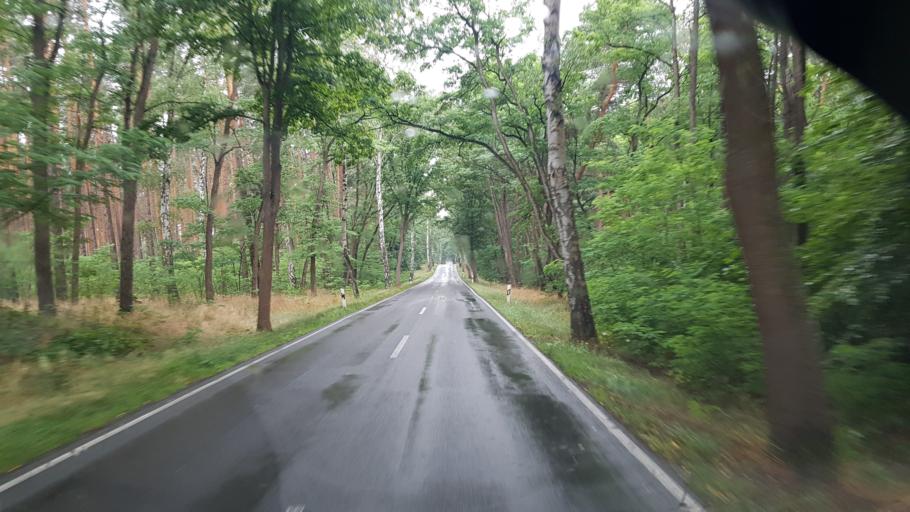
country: DE
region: Brandenburg
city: Schlieben
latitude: 51.7719
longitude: 13.3714
